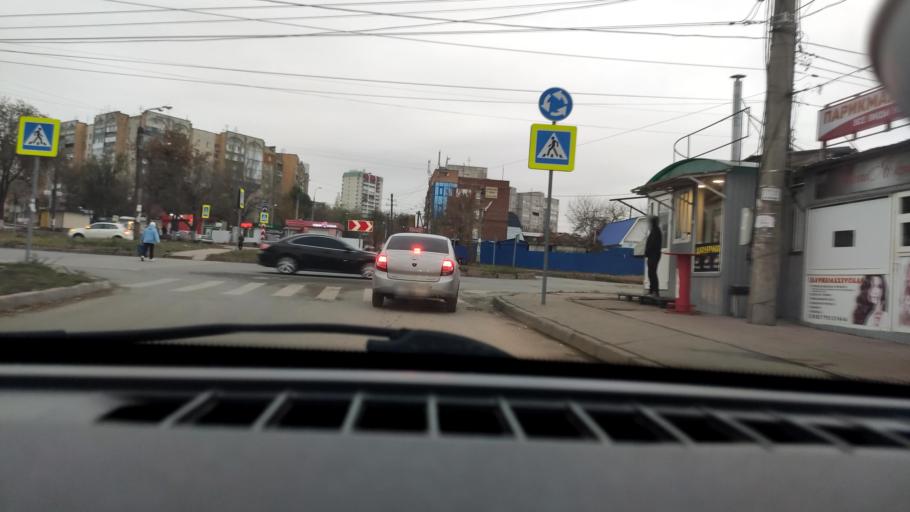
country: RU
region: Samara
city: Samara
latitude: 53.1919
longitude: 50.2137
